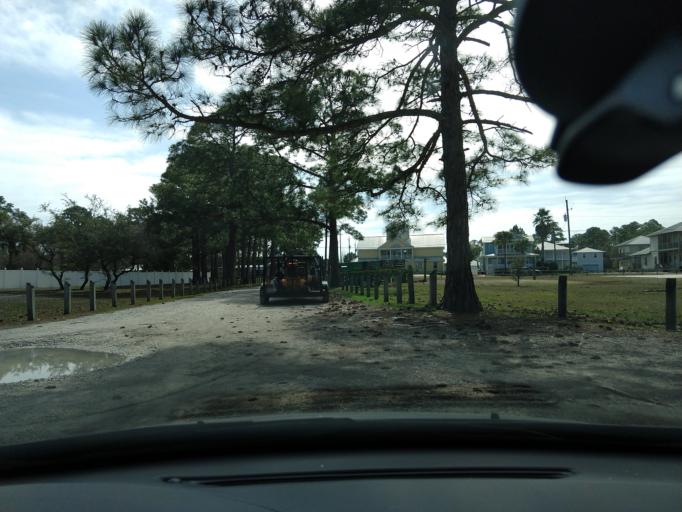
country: US
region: Florida
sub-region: Walton County
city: Miramar Beach
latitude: 30.3867
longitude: -86.3589
